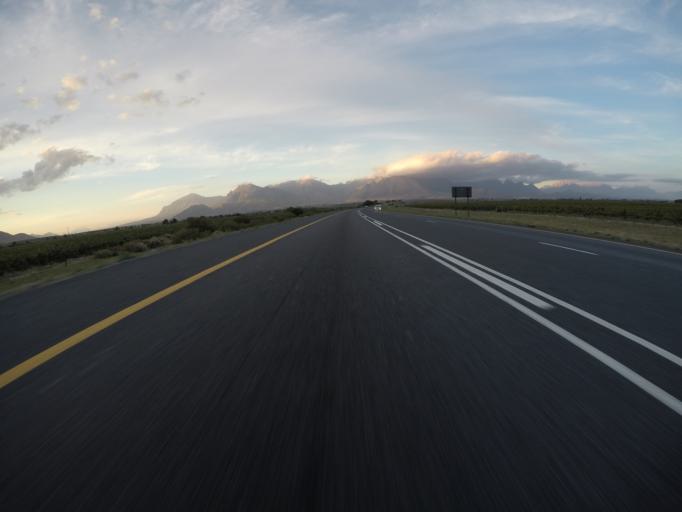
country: ZA
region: Western Cape
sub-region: Cape Winelands District Municipality
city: Worcester
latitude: -33.6581
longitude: 19.2870
